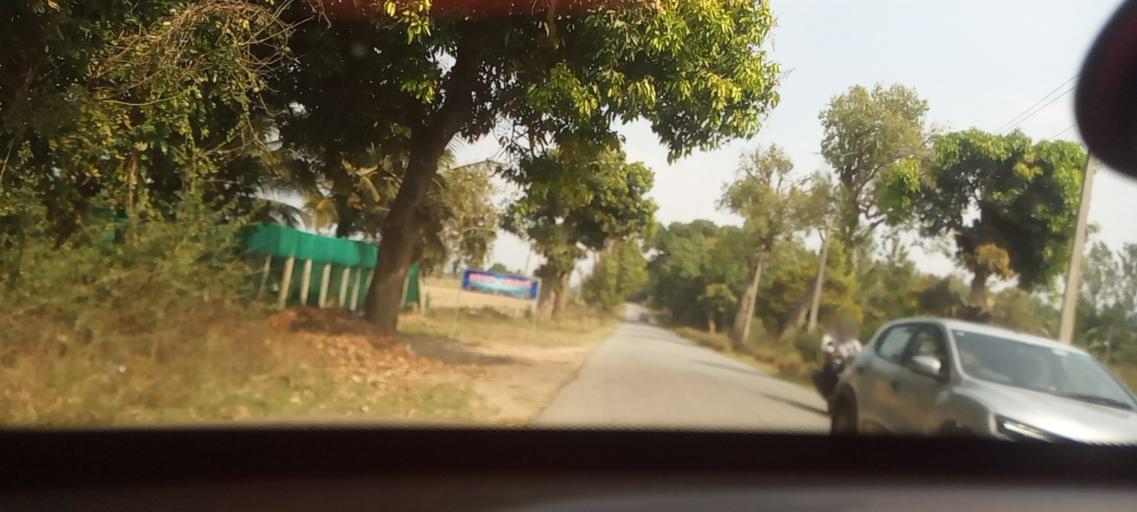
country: IN
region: Karnataka
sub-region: Hassan
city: Belur
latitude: 13.1833
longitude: 75.8370
